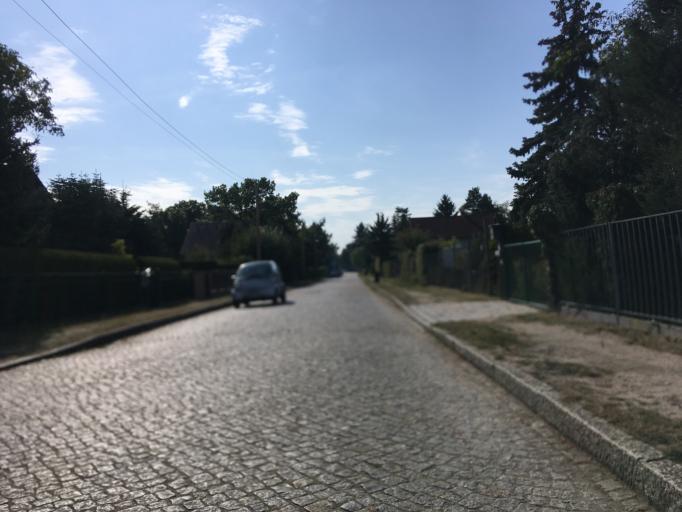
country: DE
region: Berlin
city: Mahlsdorf
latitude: 52.4943
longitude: 13.6054
